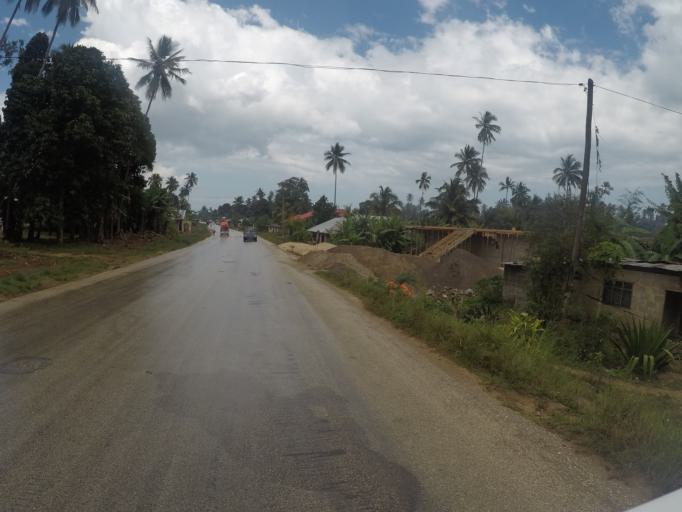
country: TZ
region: Zanzibar Central/South
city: Koani
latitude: -6.0438
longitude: 39.2280
